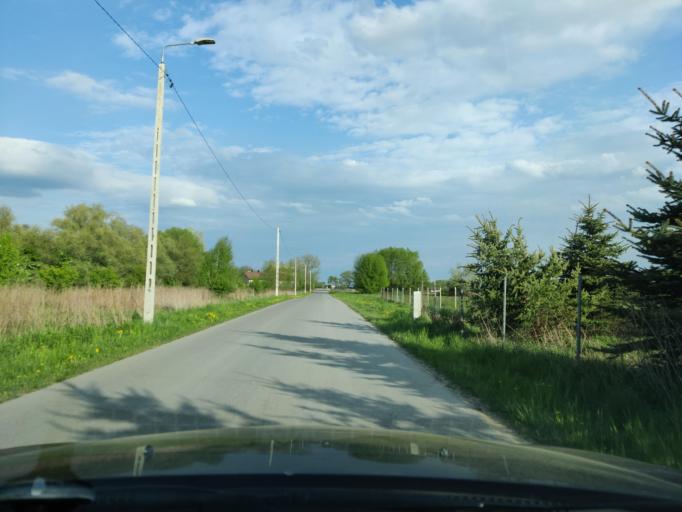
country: PL
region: Masovian Voivodeship
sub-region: Powiat piaseczynski
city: Konstancin-Jeziorna
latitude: 52.1219
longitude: 21.1593
